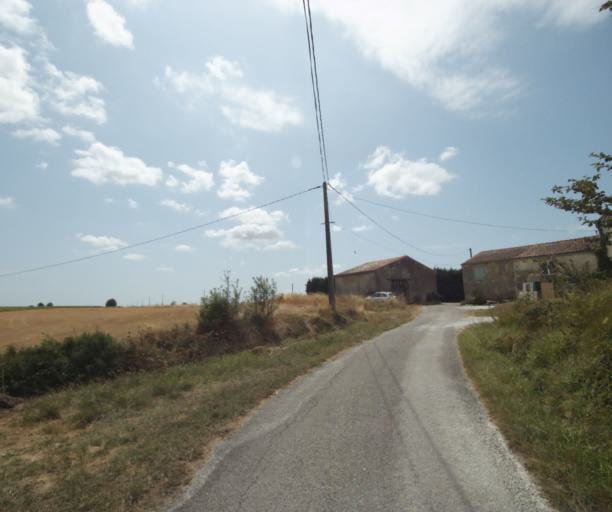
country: FR
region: Midi-Pyrenees
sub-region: Departement de la Haute-Garonne
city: Saint-Felix-Lauragais
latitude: 43.3984
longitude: 1.8987
